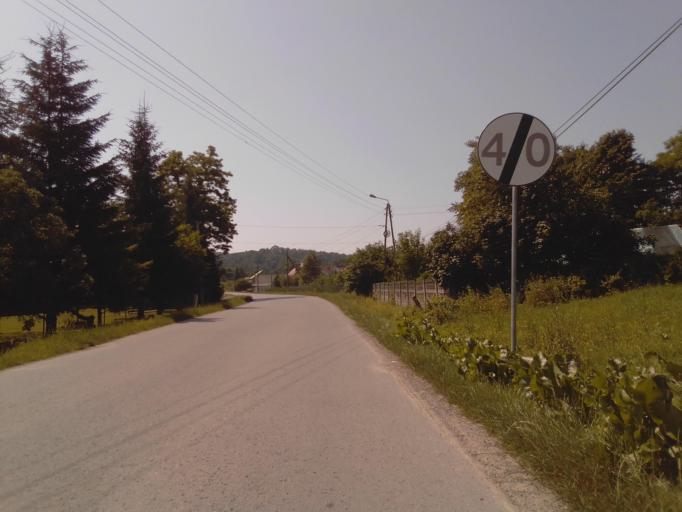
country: PL
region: Subcarpathian Voivodeship
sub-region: Powiat ropczycko-sedziszowski
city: Zagorzyce
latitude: 50.0422
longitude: 21.6554
